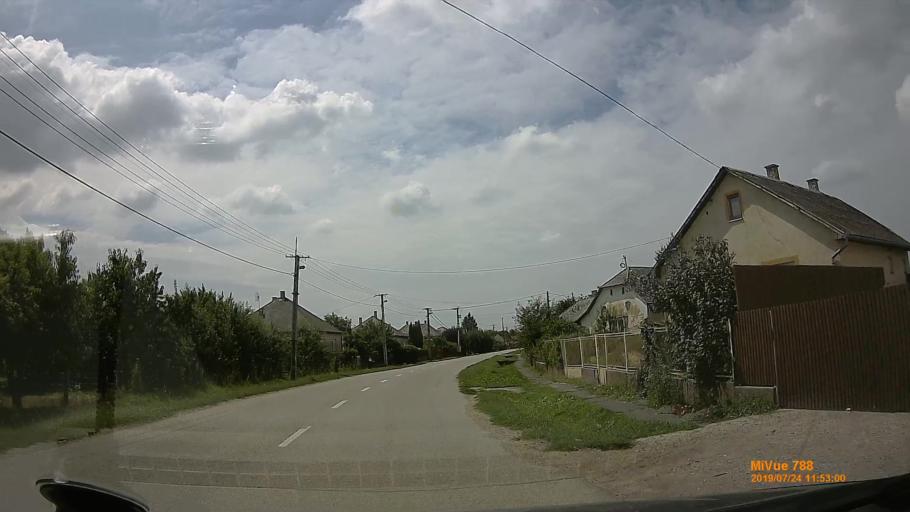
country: UA
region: Zakarpattia
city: Batiovo
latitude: 48.2293
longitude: 22.4266
